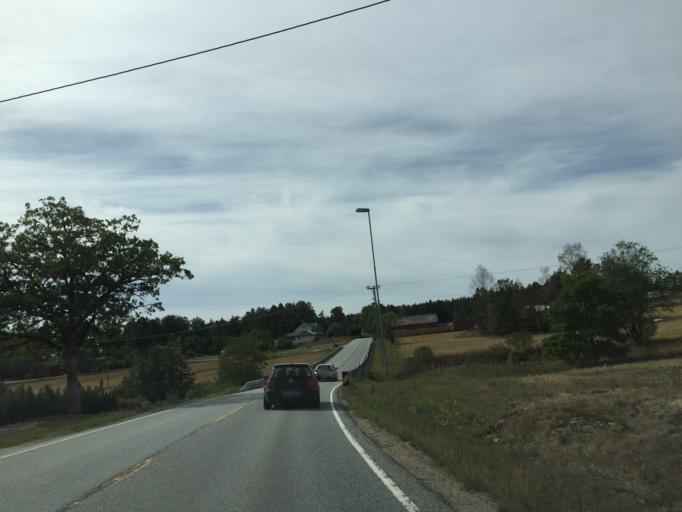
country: NO
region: Ostfold
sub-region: Fredrikstad
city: Fredrikstad
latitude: 59.2769
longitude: 10.9012
